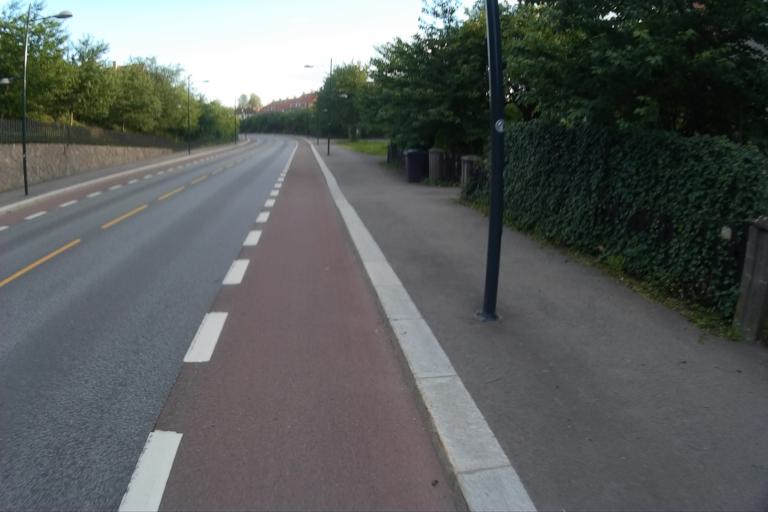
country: NO
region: Oslo
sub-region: Oslo
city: Oslo
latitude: 59.9433
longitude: 10.7304
